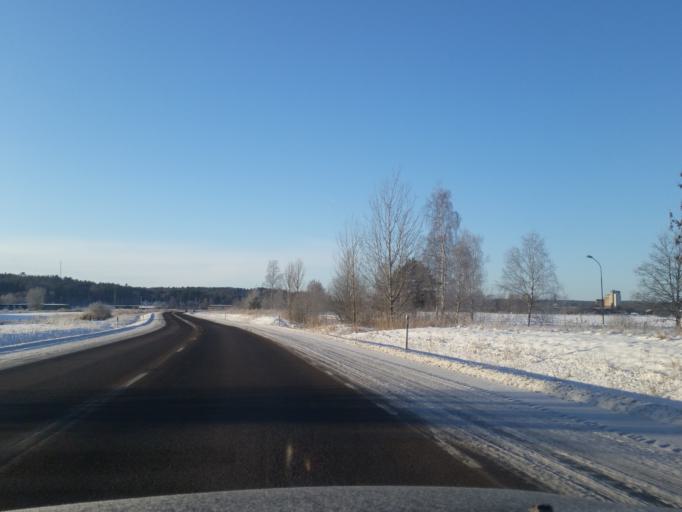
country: SE
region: Vaestmanland
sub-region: Arboga Kommun
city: Arboga
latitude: 59.3962
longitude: 15.8768
